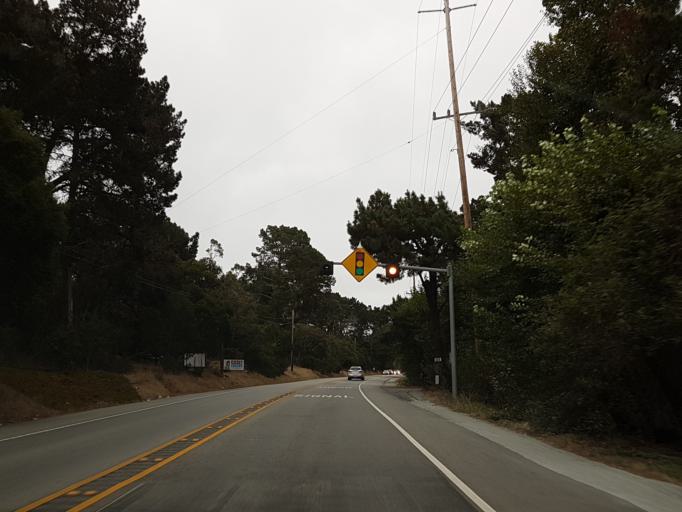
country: US
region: California
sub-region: Monterey County
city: Del Rey Oaks
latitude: 36.5854
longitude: -121.8611
